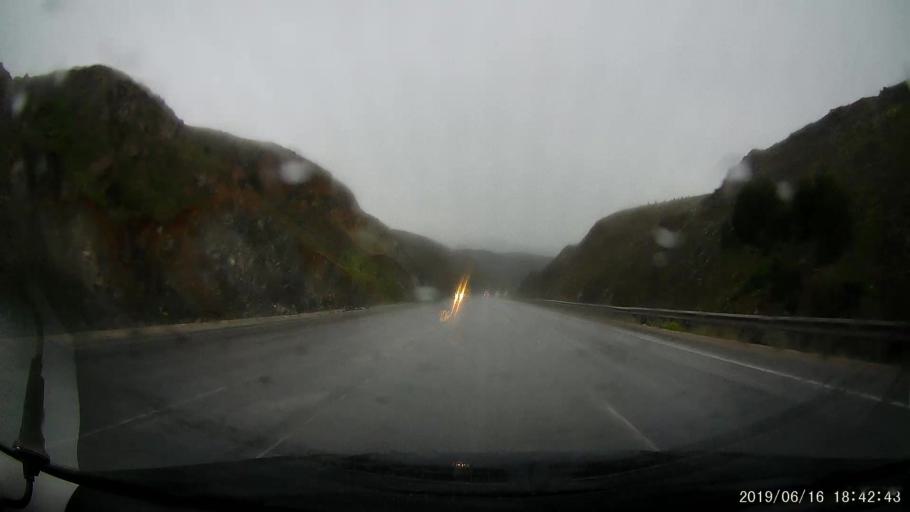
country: TR
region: Erzincan
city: Doganbeyli
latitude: 39.8682
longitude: 39.1039
